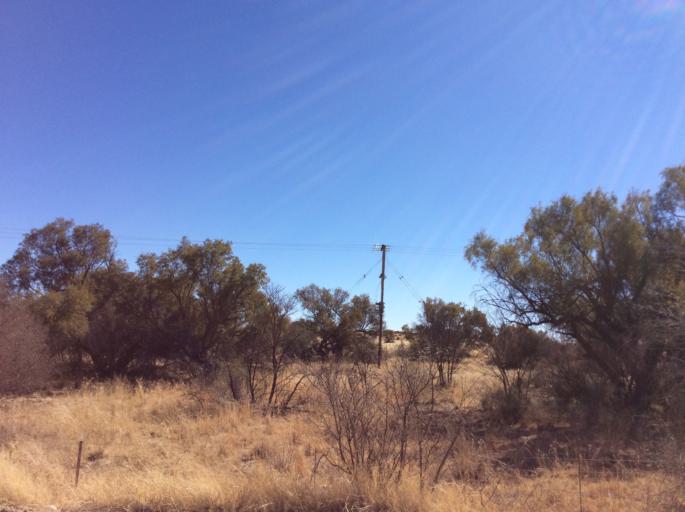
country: ZA
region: Orange Free State
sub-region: Lejweleputswa District Municipality
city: Brandfort
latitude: -28.7177
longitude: 26.0621
